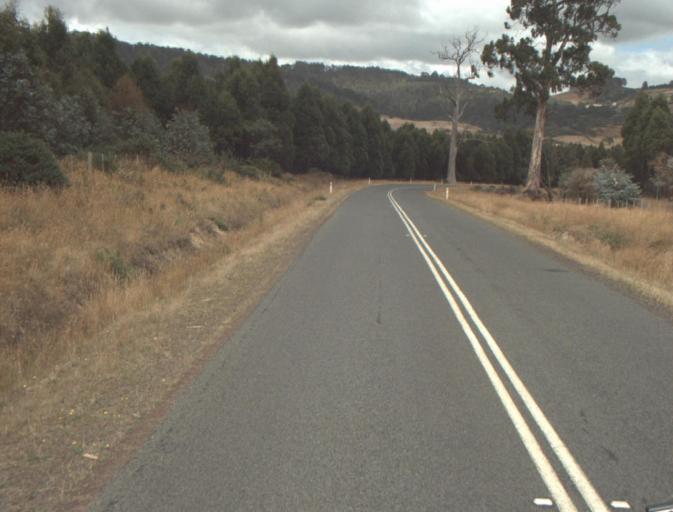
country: AU
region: Tasmania
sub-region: Northern Midlands
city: Evandale
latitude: -41.4983
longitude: 147.4957
